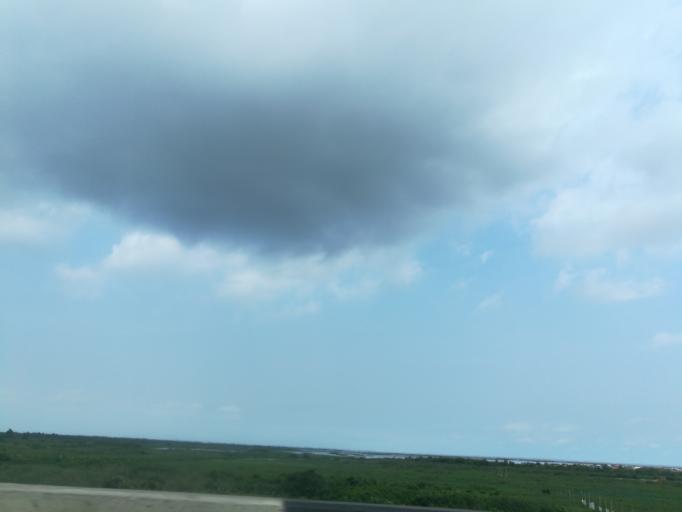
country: NG
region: Lagos
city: Ojota
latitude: 6.5661
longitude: 3.3963
